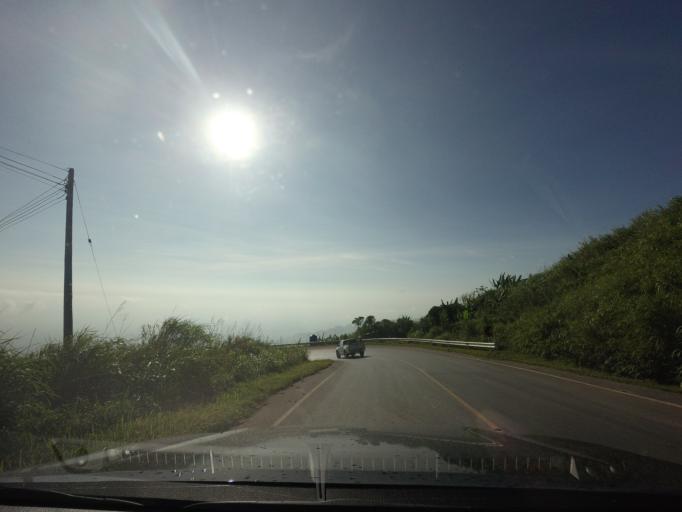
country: TH
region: Phetchabun
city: Lom Kao
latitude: 16.8843
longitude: 101.0997
